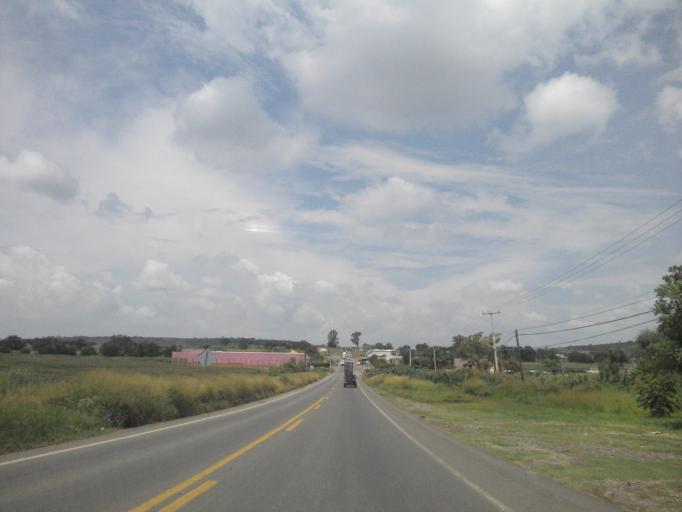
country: MX
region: Jalisco
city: Zapotlanejo
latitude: 20.6305
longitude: -103.0517
